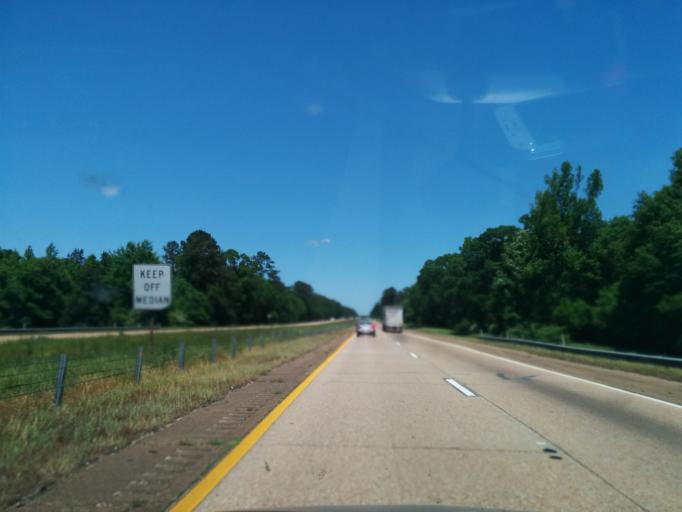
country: US
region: Mississippi
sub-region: Pike County
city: Magnolia
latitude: 31.1226
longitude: -90.4834
